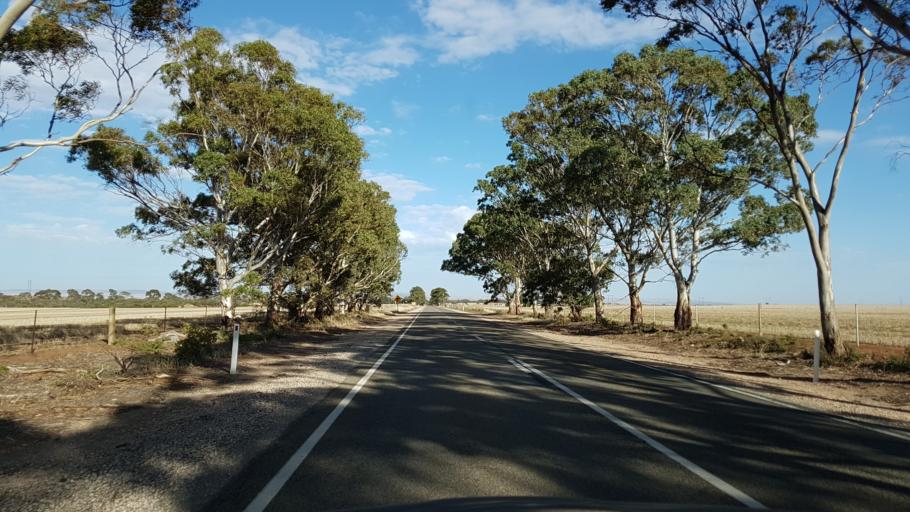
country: AU
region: South Australia
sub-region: Clare and Gilbert Valleys
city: Clare
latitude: -33.6957
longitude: 138.4350
